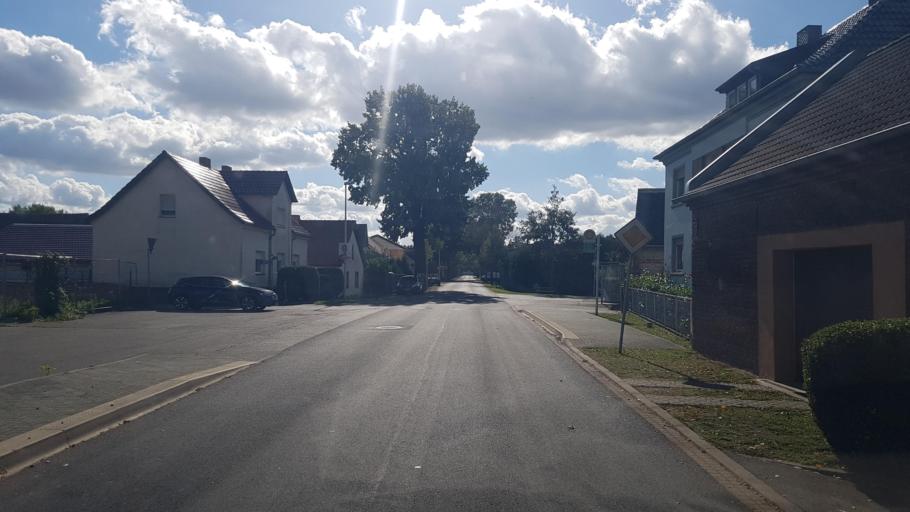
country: DE
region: Brandenburg
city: Peitz
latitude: 51.8110
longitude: 14.3856
